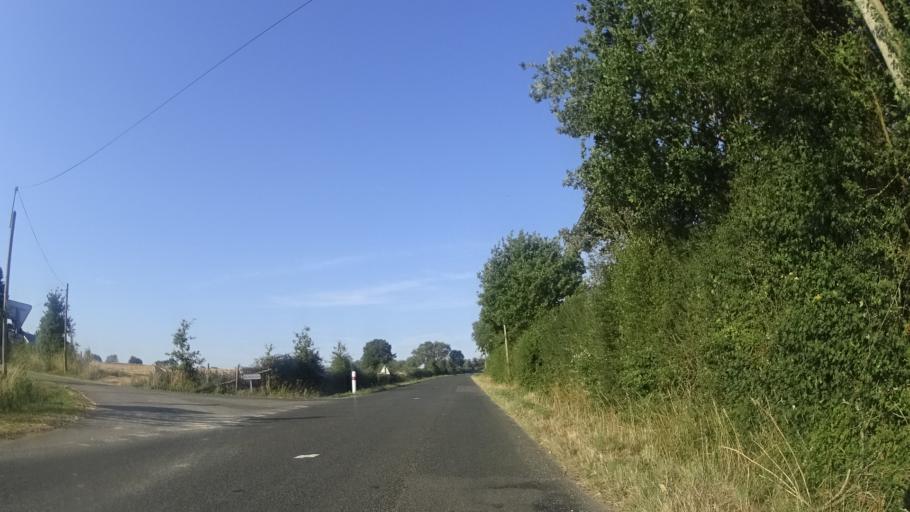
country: FR
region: Pays de la Loire
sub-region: Departement de la Loire-Atlantique
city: Riaille
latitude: 47.5003
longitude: -1.3088
